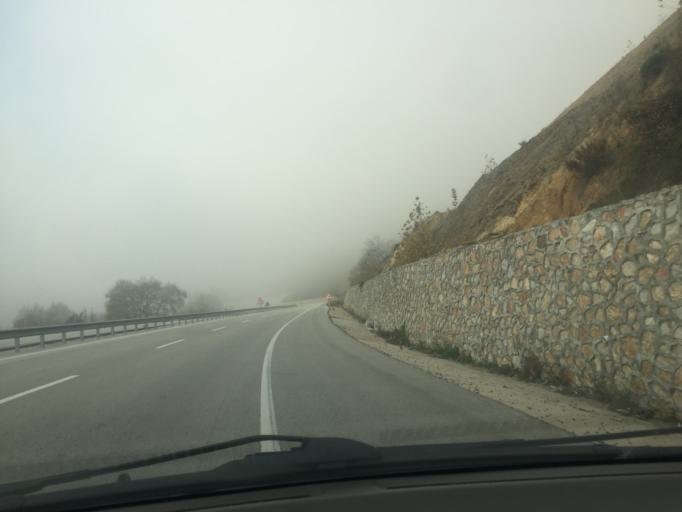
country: TR
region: Canakkale
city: Biga
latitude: 40.1381
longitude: 27.2031
